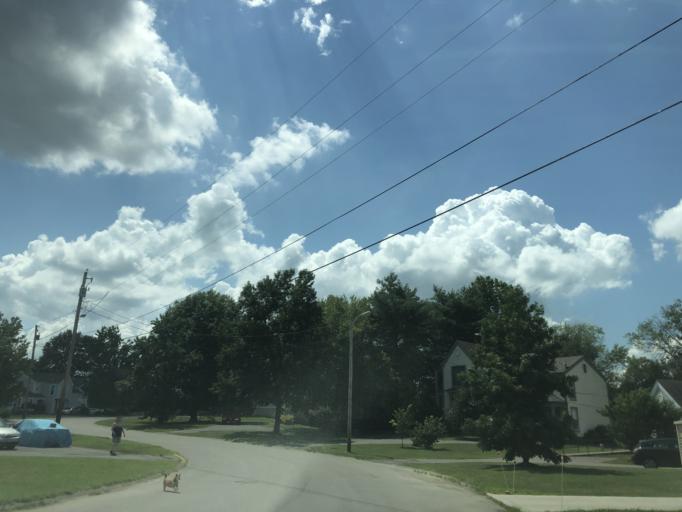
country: US
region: Tennessee
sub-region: Davidson County
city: Lakewood
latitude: 36.2027
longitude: -86.6054
